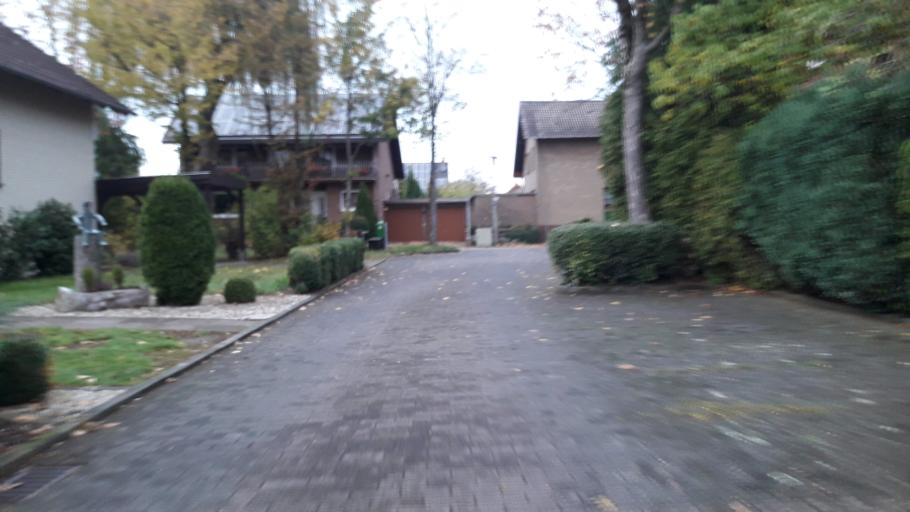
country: DE
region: North Rhine-Westphalia
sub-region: Regierungsbezirk Detmold
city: Delbruck
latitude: 51.7391
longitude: 8.6251
